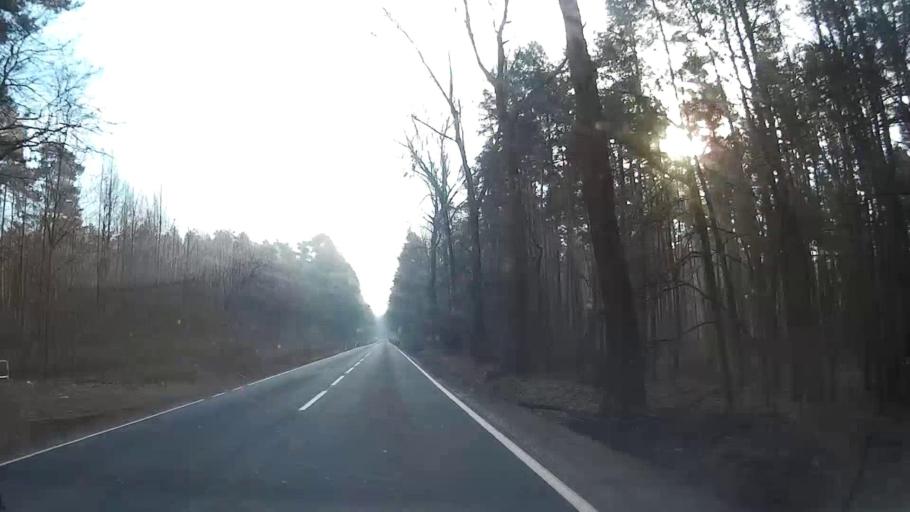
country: PL
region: Lesser Poland Voivodeship
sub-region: Powiat chrzanowski
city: Zagorze
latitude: 50.0729
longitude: 19.3940
